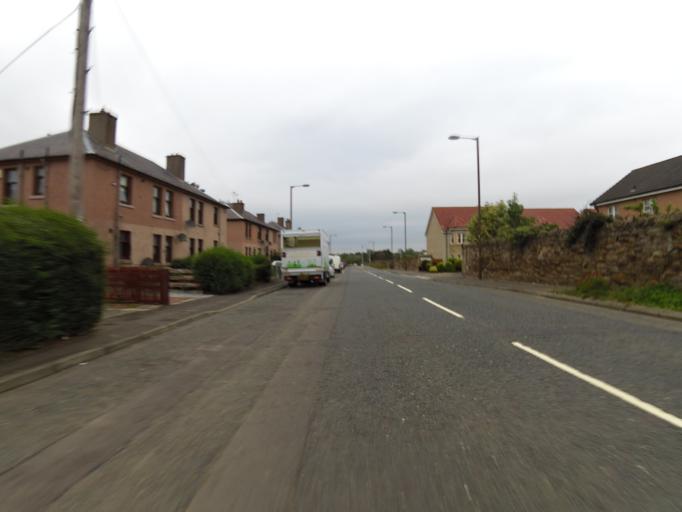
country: GB
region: Scotland
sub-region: East Lothian
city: Musselburgh
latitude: 55.9224
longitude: -3.0671
